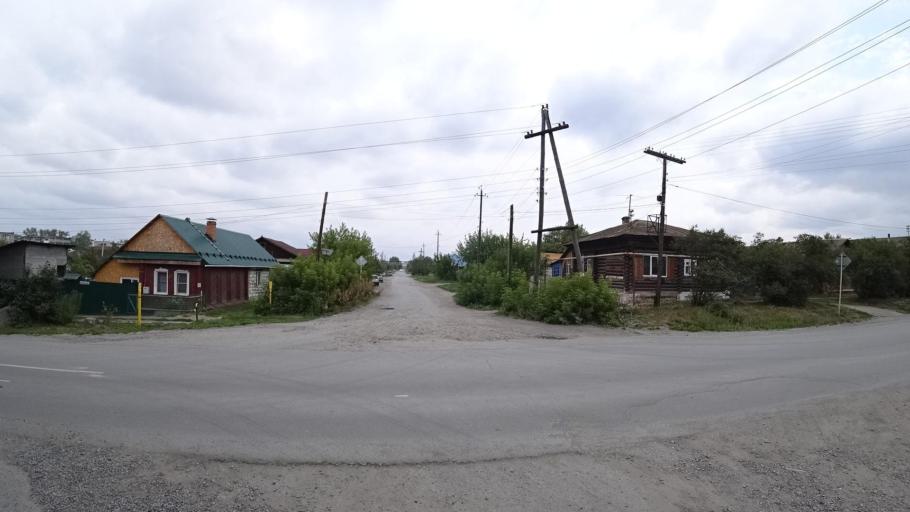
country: RU
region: Sverdlovsk
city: Kamyshlov
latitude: 56.8365
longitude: 62.7164
